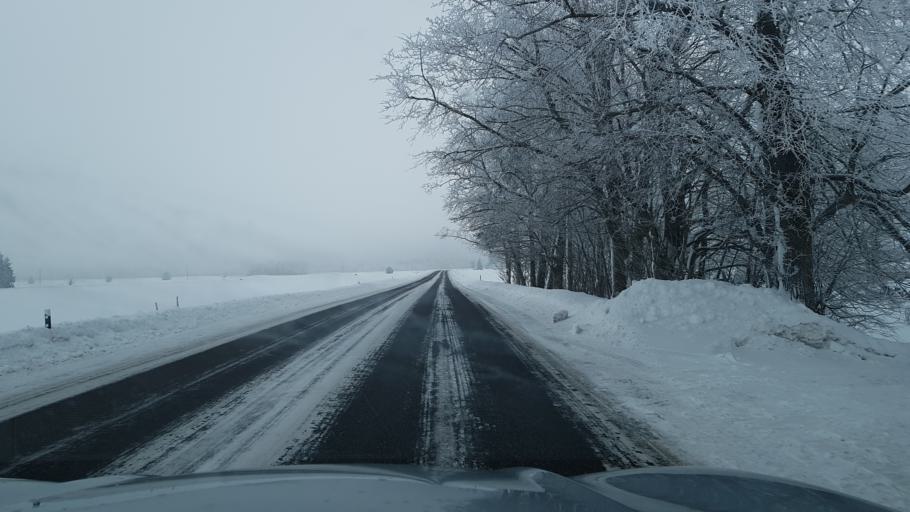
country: EE
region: Ida-Virumaa
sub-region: Johvi vald
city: Johvi
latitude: 59.2627
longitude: 27.3839
